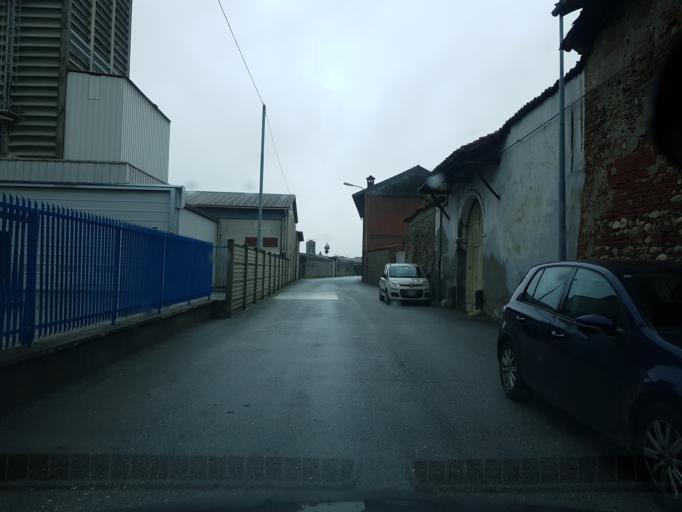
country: IT
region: Piedmont
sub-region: Provincia di Cuneo
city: Villafalletto
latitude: 44.5463
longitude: 7.5412
